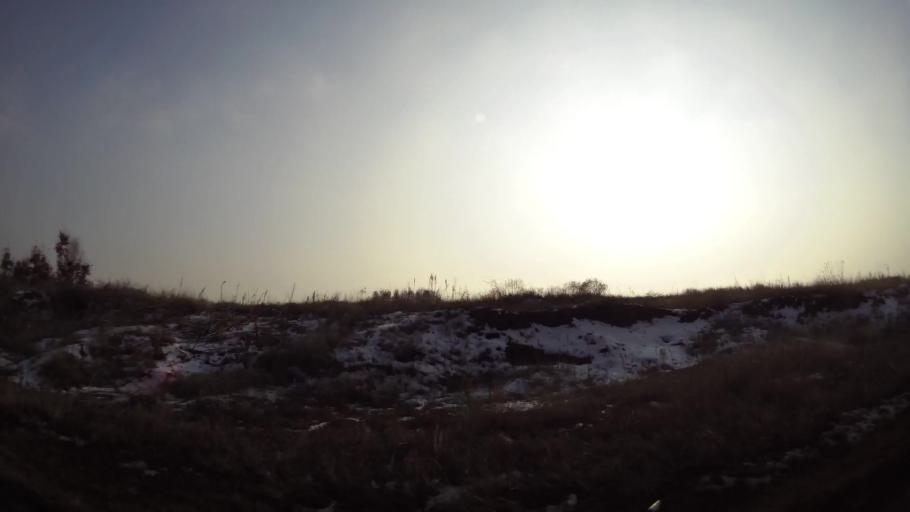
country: MK
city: Kadino
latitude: 41.9779
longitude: 21.6233
